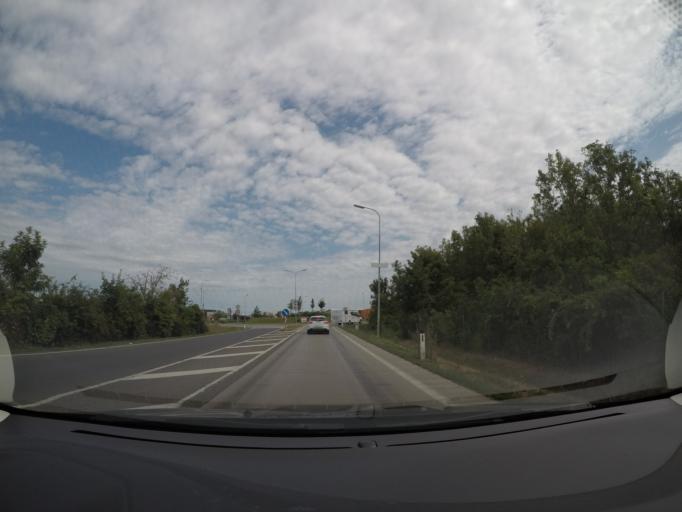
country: AT
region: Lower Austria
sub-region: Politischer Bezirk Modling
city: Wiener Neudorf
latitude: 48.1041
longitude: 16.3101
